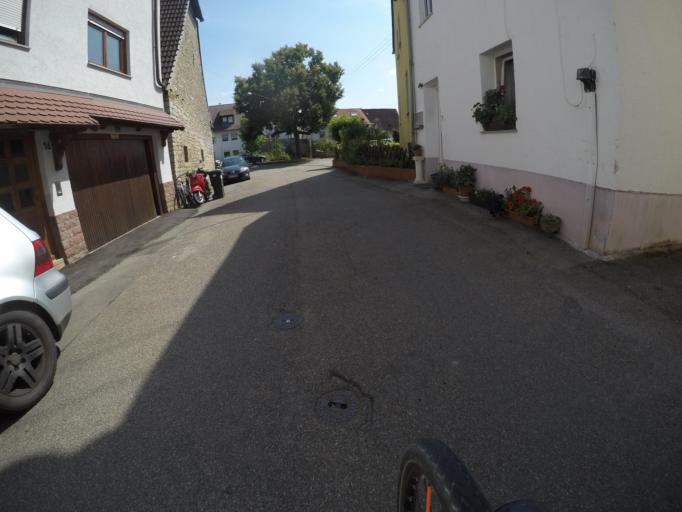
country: DE
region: Baden-Wuerttemberg
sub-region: Karlsruhe Region
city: Gondelsheim
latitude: 49.0416
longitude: 8.6773
